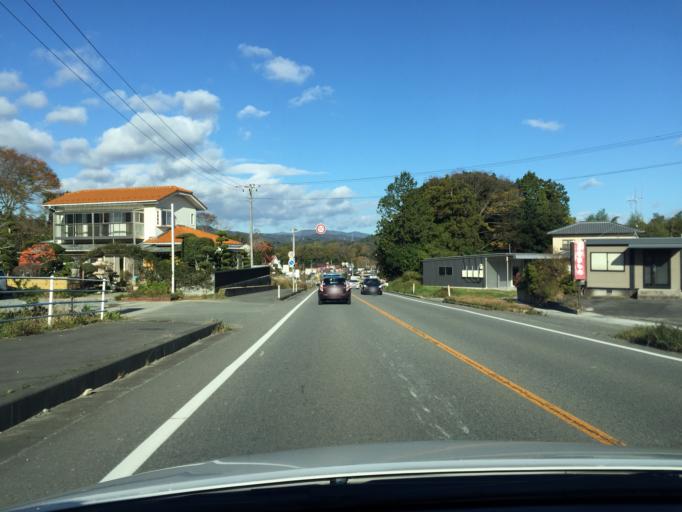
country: JP
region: Fukushima
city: Iwaki
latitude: 37.1984
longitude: 140.9961
